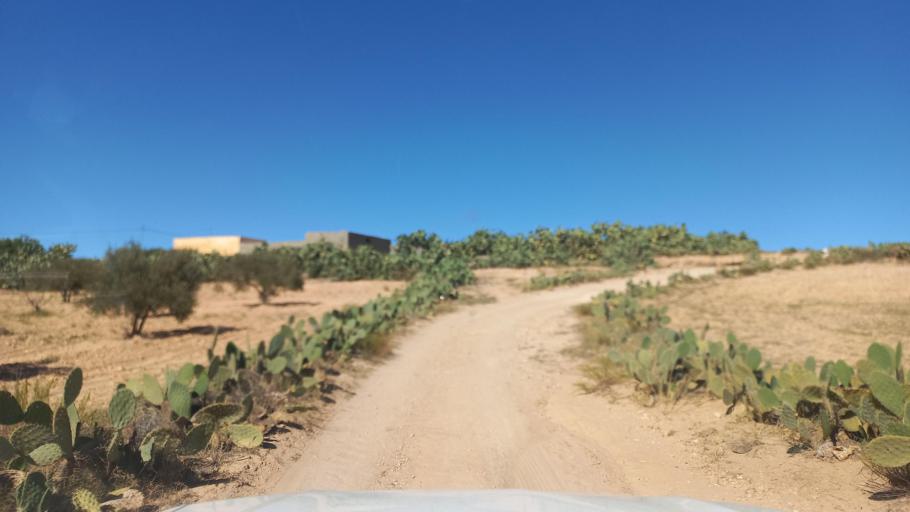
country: TN
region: Al Qasrayn
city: Sbiba
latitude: 35.3819
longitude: 9.0905
